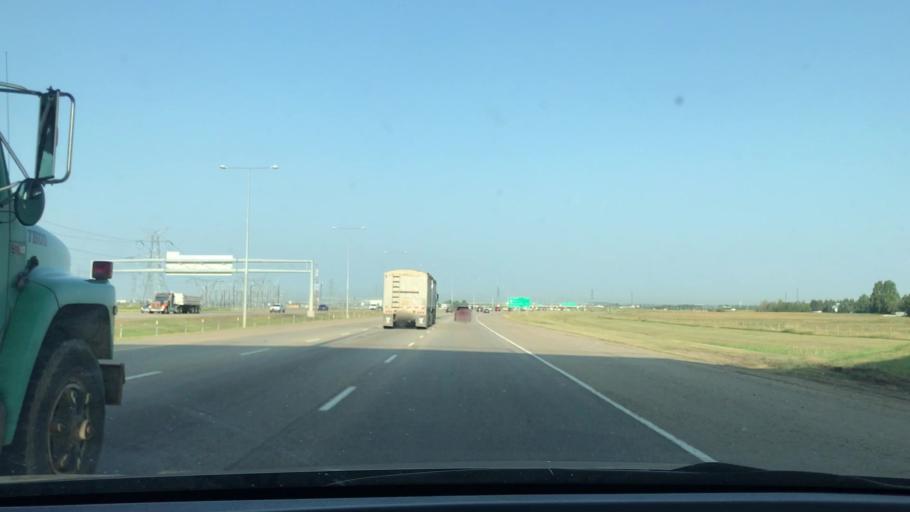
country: CA
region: Alberta
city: Beaumont
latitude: 53.4359
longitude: -113.4413
